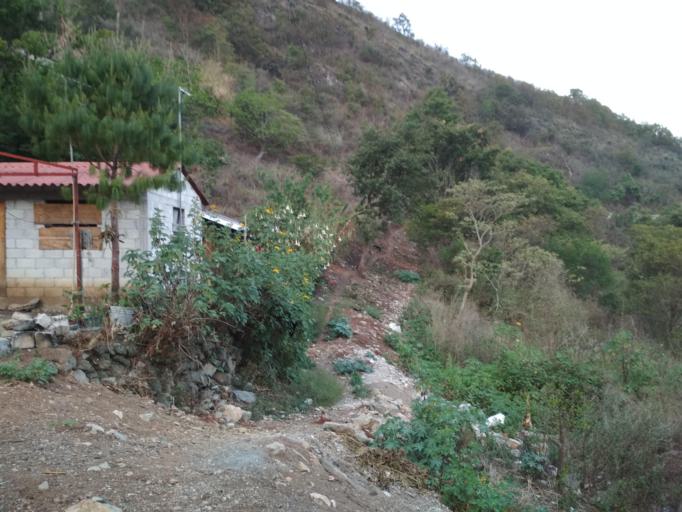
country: MX
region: Veracruz
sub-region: Nogales
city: Taza de Agua Ojo Zarco
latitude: 18.7745
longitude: -97.1896
